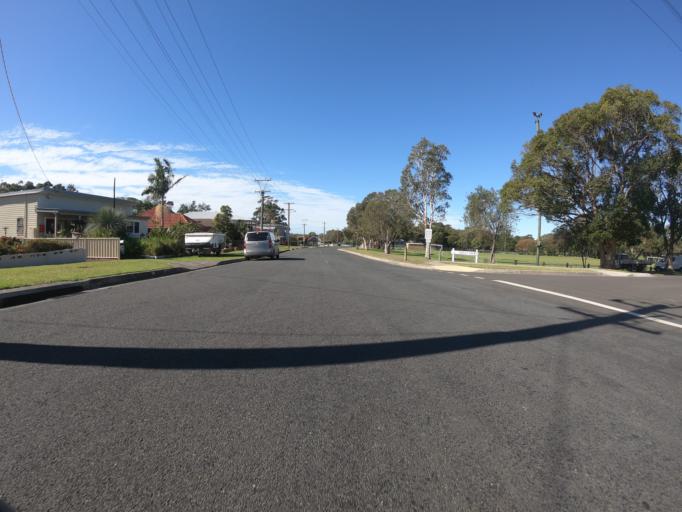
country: AU
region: New South Wales
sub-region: Wollongong
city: East Corrimal
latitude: -34.3584
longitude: 150.9039
